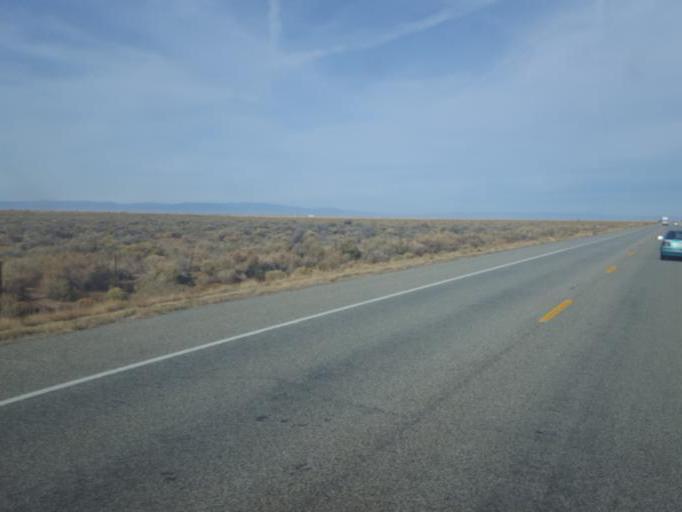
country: US
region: Colorado
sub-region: Costilla County
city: San Luis
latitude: 37.4498
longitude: -105.5419
